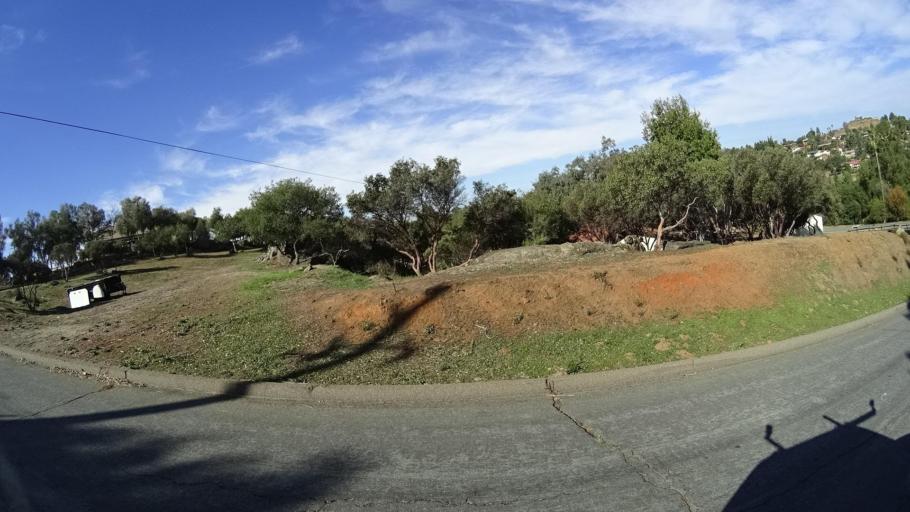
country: US
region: California
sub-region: San Diego County
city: Alpine
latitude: 32.8212
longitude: -116.7457
